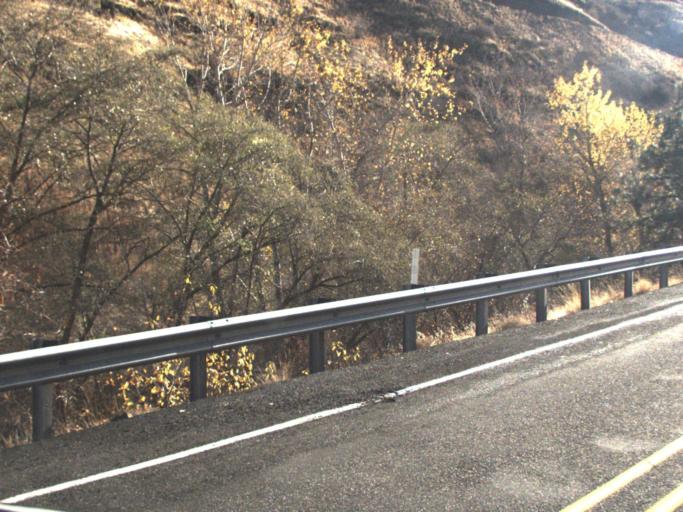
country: US
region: Washington
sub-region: Asotin County
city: Asotin
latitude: 46.0044
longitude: -117.2801
